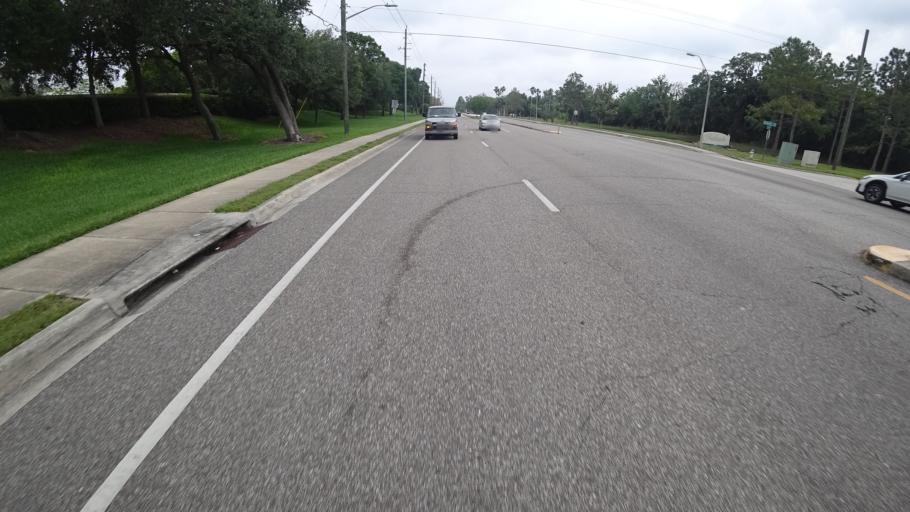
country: US
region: Florida
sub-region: Sarasota County
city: North Sarasota
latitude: 27.3960
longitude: -82.5056
